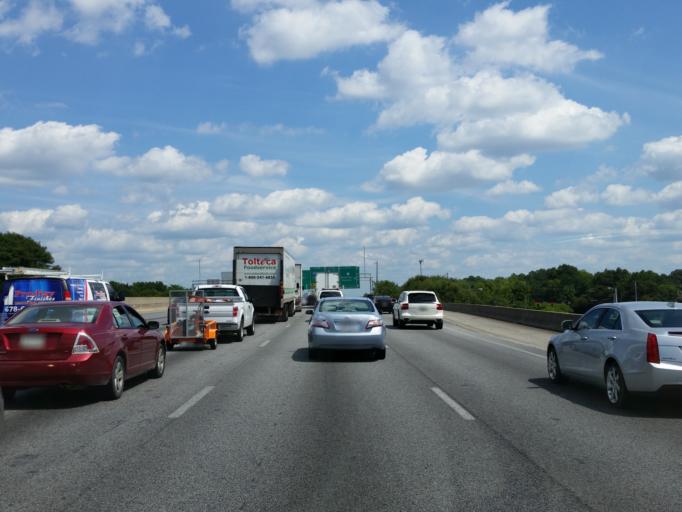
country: US
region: Georgia
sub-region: DeKalb County
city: Doraville
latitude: 33.9037
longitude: -84.2757
